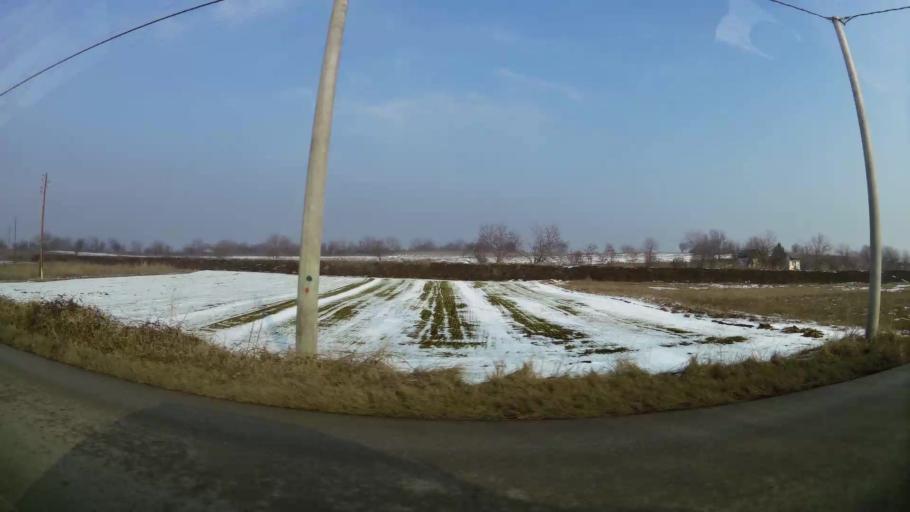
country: MK
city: Kadino
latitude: 41.9746
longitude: 21.6037
